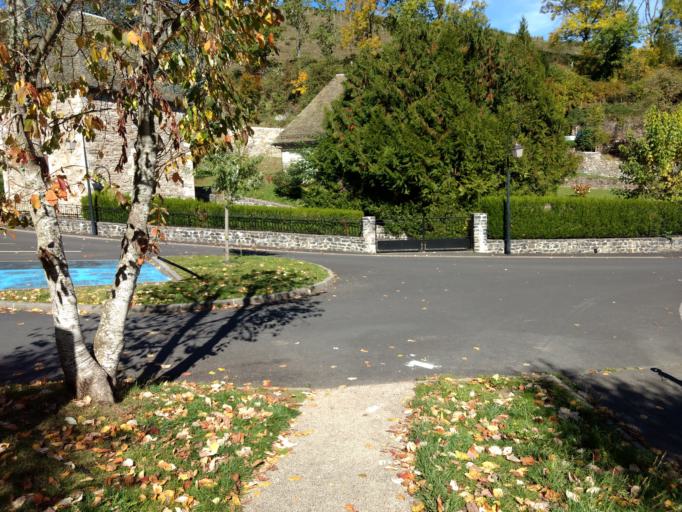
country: FR
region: Auvergne
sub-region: Departement du Cantal
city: Chaudes-Aigues
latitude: 44.8556
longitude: 3.0027
